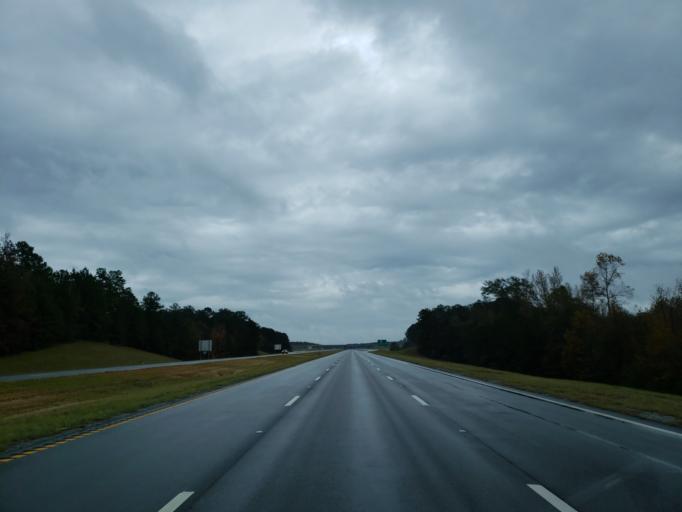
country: US
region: Mississippi
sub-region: Wayne County
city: Waynesboro
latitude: 31.7056
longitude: -88.6380
